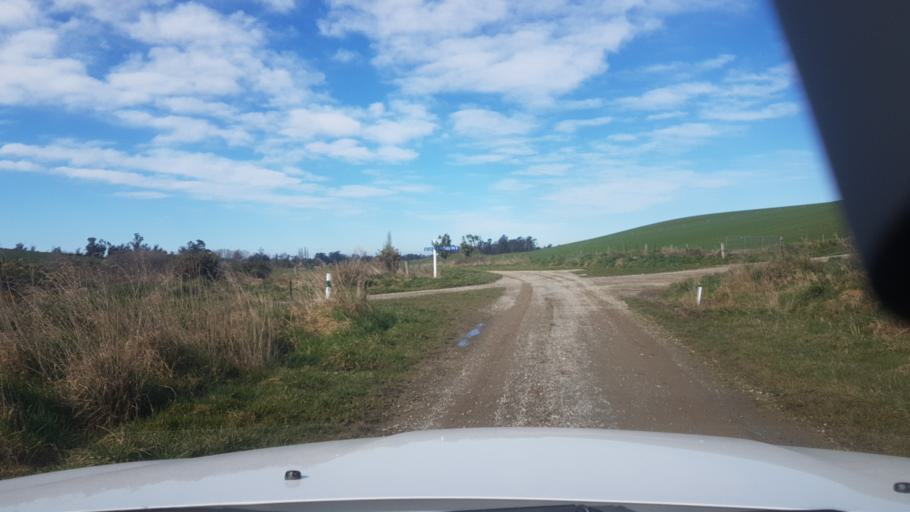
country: NZ
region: Canterbury
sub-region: Timaru District
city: Pleasant Point
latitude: -44.2020
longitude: 171.1864
